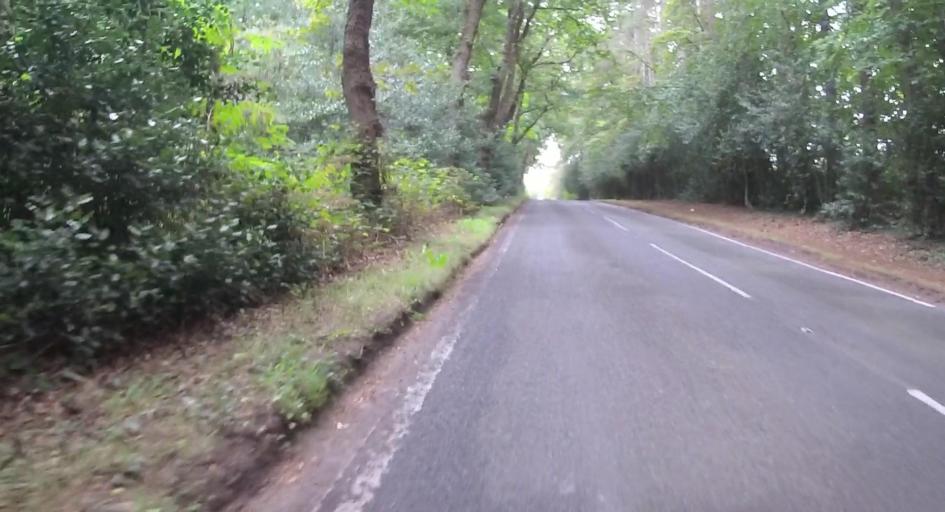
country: GB
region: England
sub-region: Surrey
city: West Byfleet
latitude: 51.3202
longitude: -0.5165
